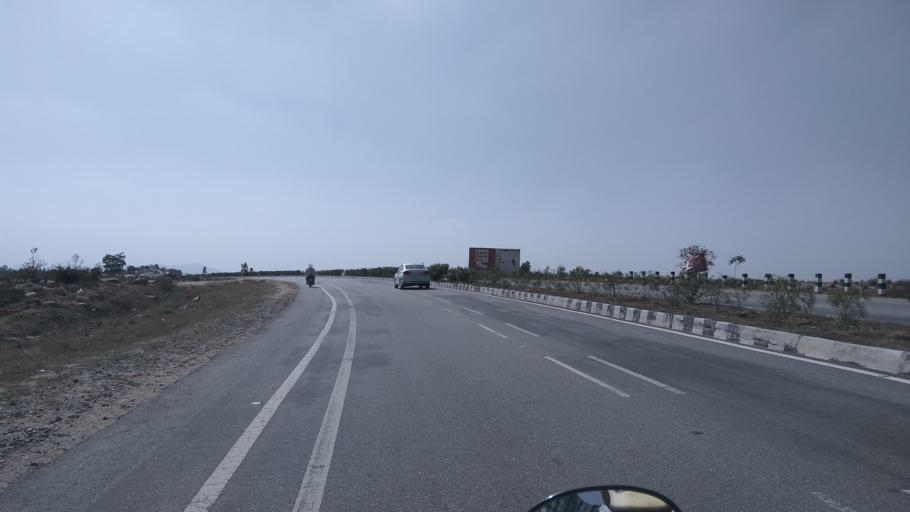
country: IN
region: Karnataka
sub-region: Kolar
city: Mulbagal
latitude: 13.1541
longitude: 78.3089
